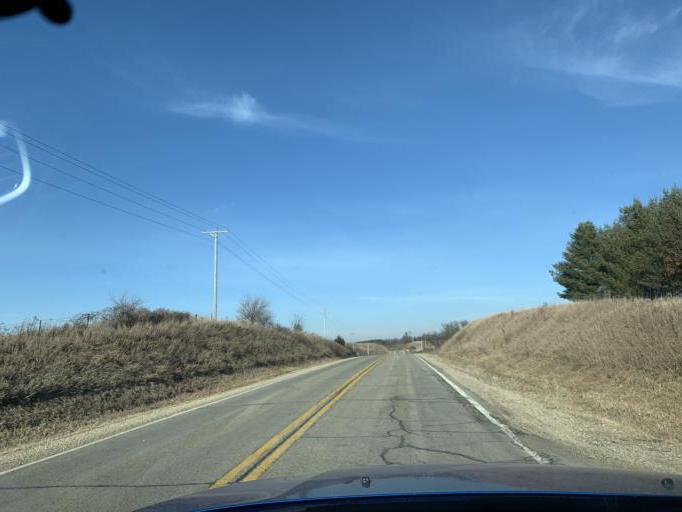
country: US
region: Wisconsin
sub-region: Green County
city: New Glarus
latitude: 42.7739
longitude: -89.8581
